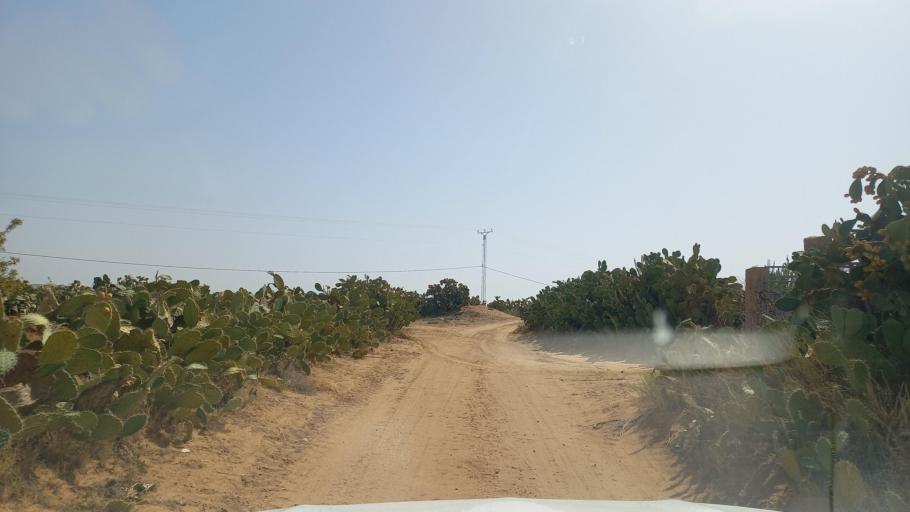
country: TN
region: Al Qasrayn
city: Kasserine
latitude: 35.2404
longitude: 9.0692
